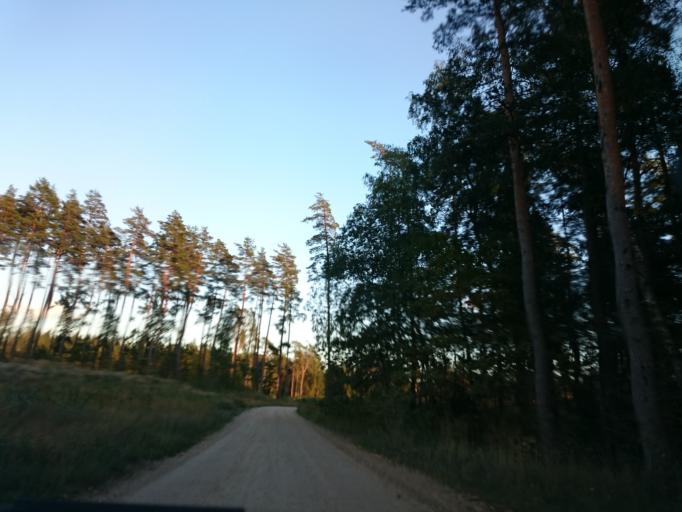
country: LV
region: Adazi
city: Adazi
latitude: 57.0630
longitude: 24.2795
